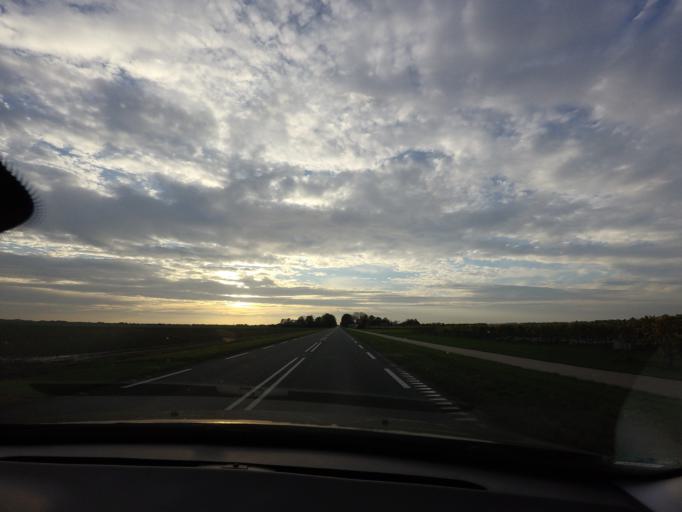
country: NL
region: Overijssel
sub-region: Gemeente Steenwijkerland
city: Blokzijl
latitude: 52.7211
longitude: 5.9244
